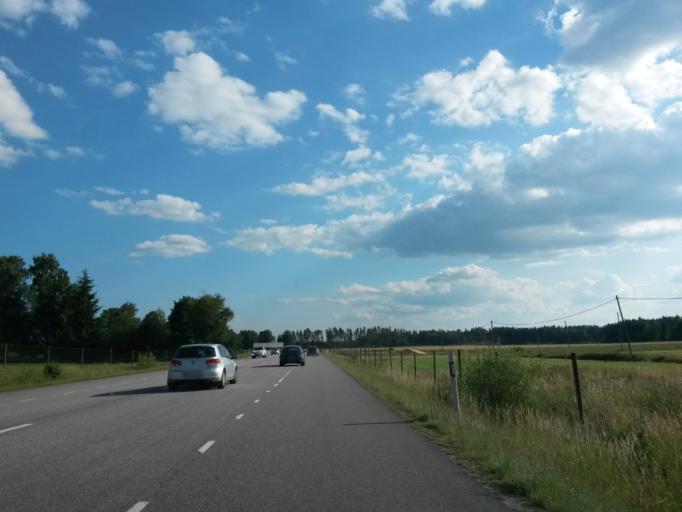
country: SE
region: Vaestra Goetaland
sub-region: Vara Kommun
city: Vara
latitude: 58.2019
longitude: 12.8984
